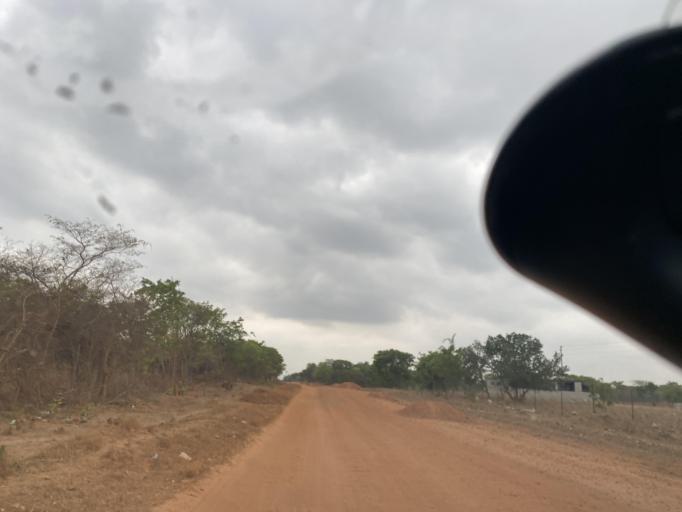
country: ZM
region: Lusaka
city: Chongwe
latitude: -15.2749
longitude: 28.7308
